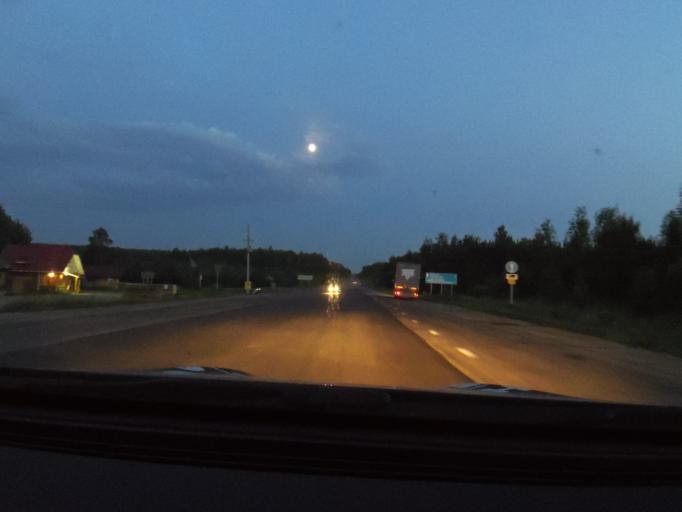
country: RU
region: Bashkortostan
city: Duvan
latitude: 56.0049
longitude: 58.2130
